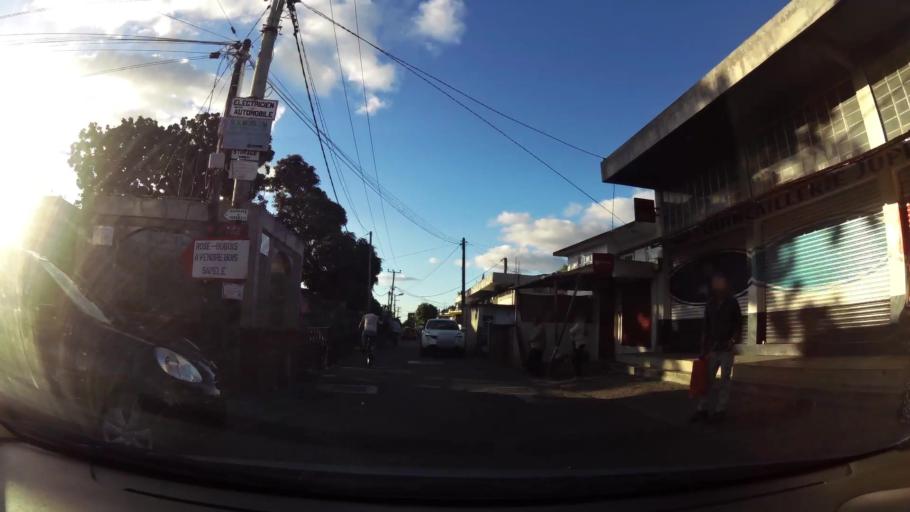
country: MU
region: Plaines Wilhems
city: Quatre Bornes
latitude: -20.2480
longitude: 57.4617
